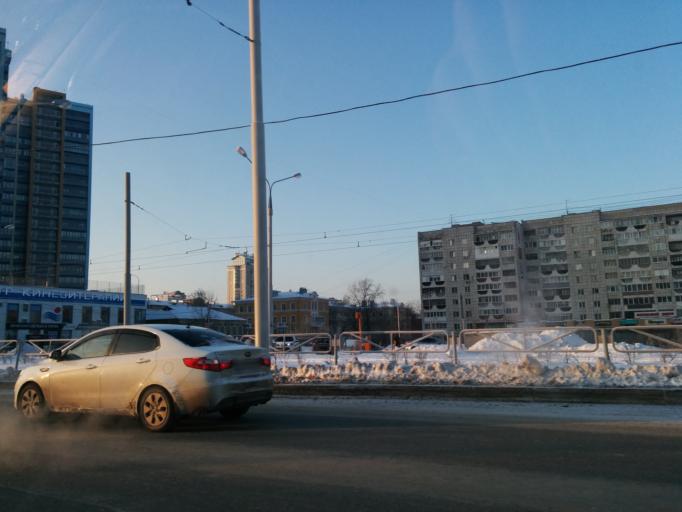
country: RU
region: Perm
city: Perm
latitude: 58.0060
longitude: 56.2586
